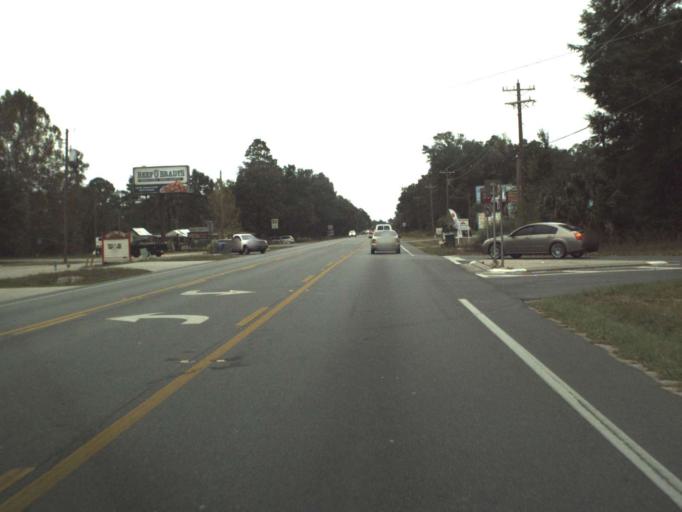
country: US
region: Florida
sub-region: Wakulla County
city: Crawfordville
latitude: 30.1984
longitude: -84.3695
